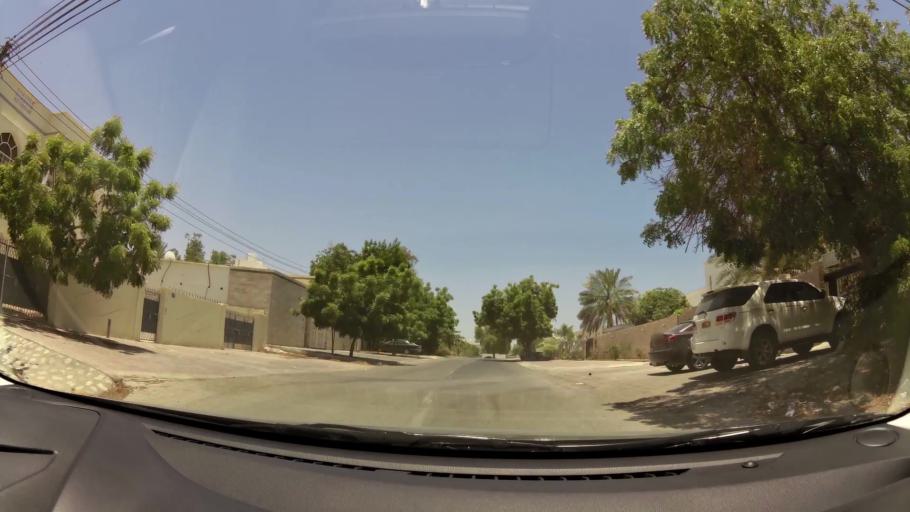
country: OM
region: Muhafazat Masqat
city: As Sib al Jadidah
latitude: 23.6307
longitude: 58.2374
